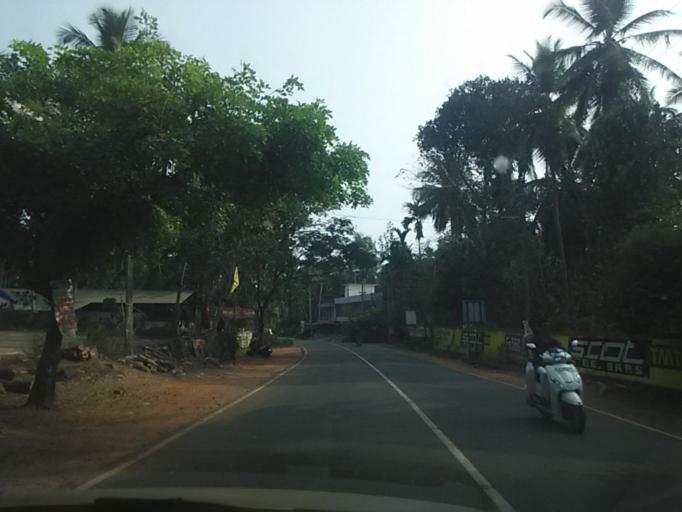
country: IN
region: Kerala
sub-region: Kozhikode
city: Naduvannur
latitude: 11.4805
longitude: 75.7747
